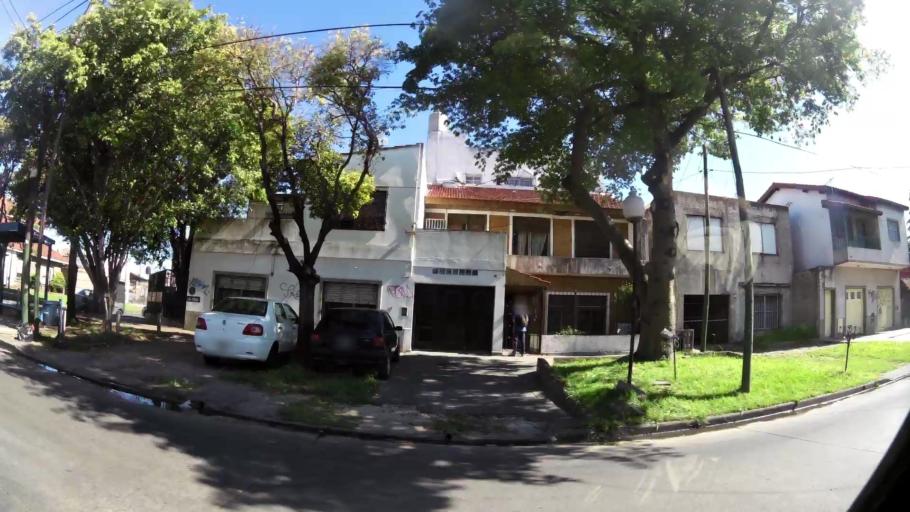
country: AR
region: Buenos Aires
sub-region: Partido de Lomas de Zamora
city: Lomas de Zamora
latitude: -34.7478
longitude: -58.4138
